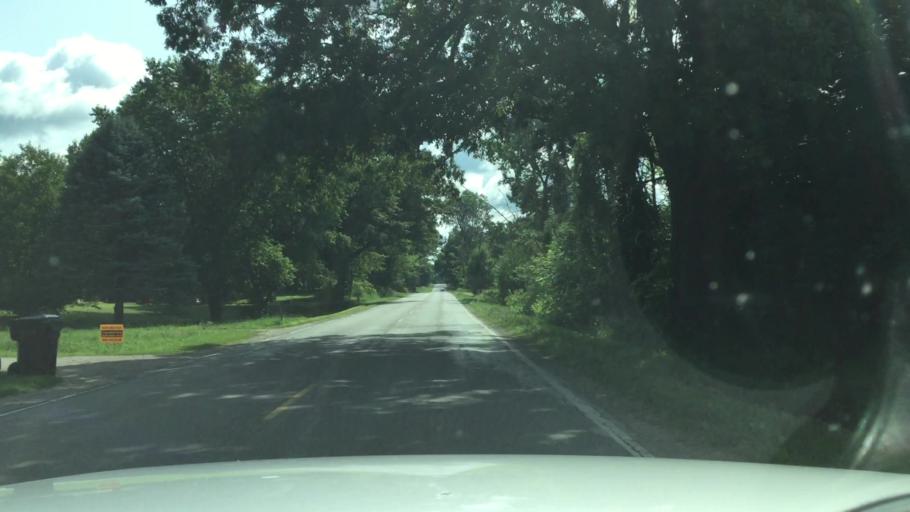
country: US
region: Michigan
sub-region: Montcalm County
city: Greenville
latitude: 43.1920
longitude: -85.1864
